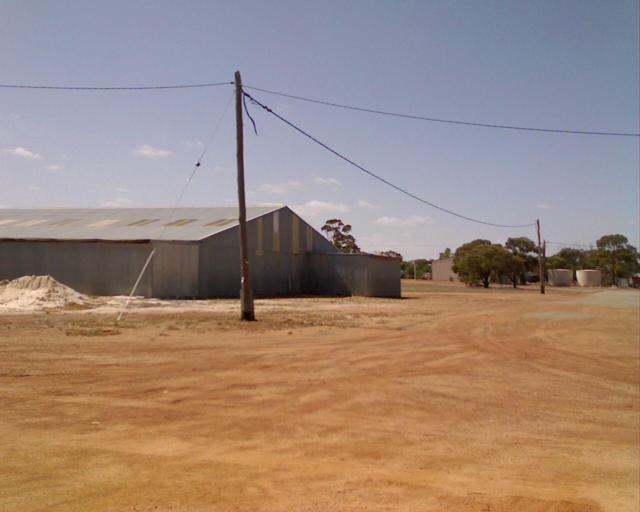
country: AU
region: Western Australia
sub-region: Merredin
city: Merredin
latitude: -30.9123
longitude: 118.2066
